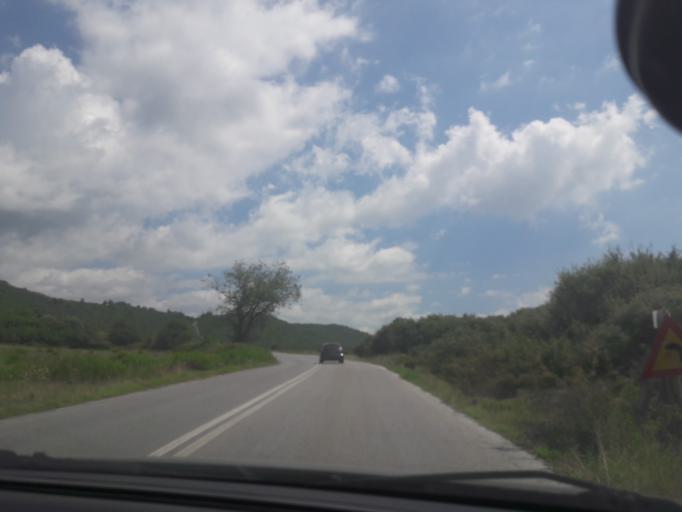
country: GR
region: Central Macedonia
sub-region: Nomos Chalkidikis
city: Polygyros
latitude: 40.3655
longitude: 23.4198
